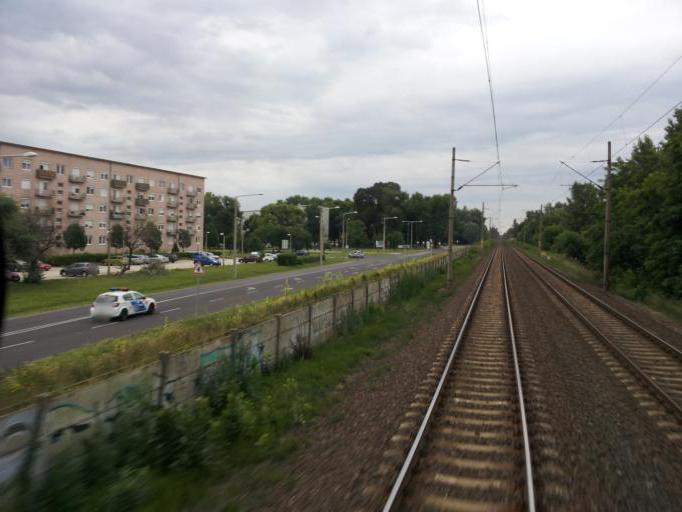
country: HU
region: Fejer
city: Szekesfehervar
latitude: 47.1462
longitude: 18.4079
